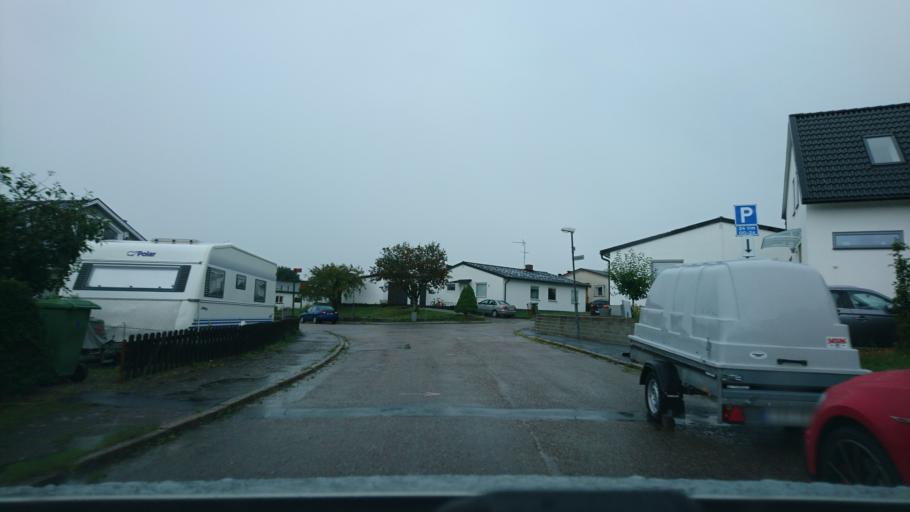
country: SE
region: Uppsala
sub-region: Uppsala Kommun
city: Gamla Uppsala
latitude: 59.8796
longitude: 17.6125
